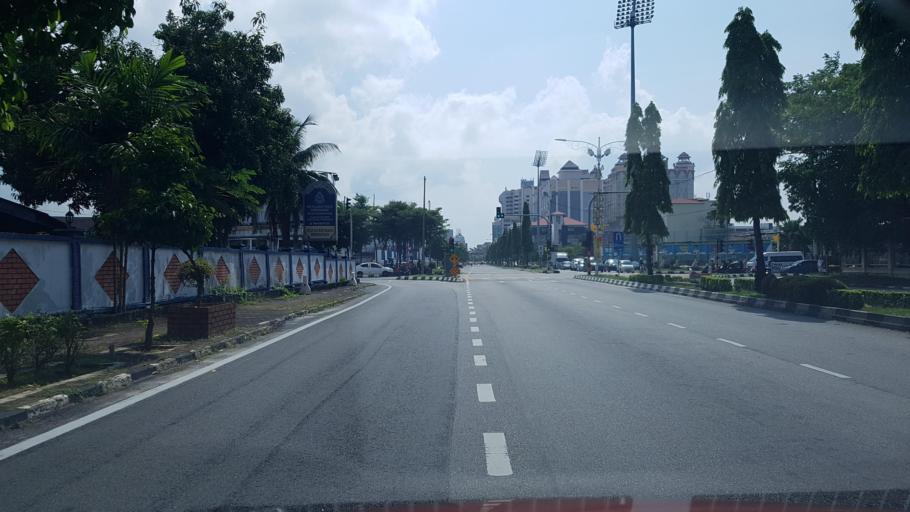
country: MY
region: Terengganu
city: Kuala Terengganu
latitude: 5.3280
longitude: 103.1418
